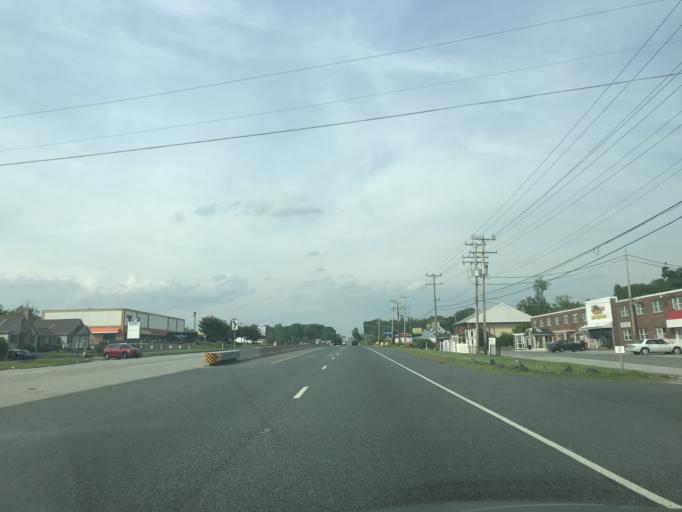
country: US
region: Maryland
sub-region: Baltimore County
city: White Marsh
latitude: 39.3859
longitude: -76.4201
